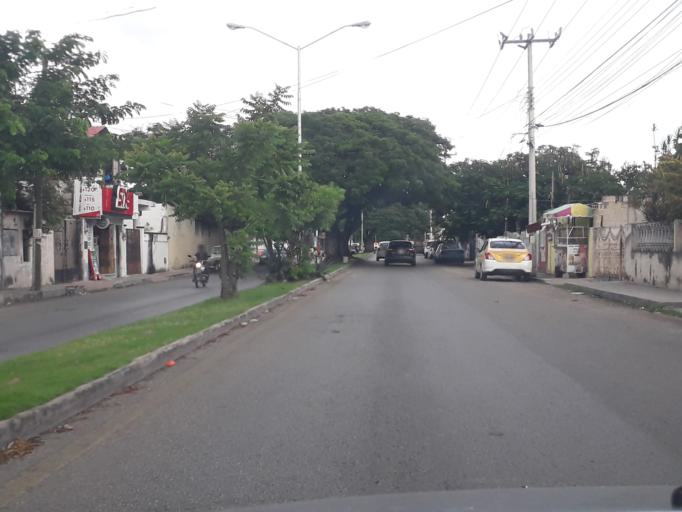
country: MX
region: Yucatan
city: Merida
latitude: 20.9619
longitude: -89.6614
